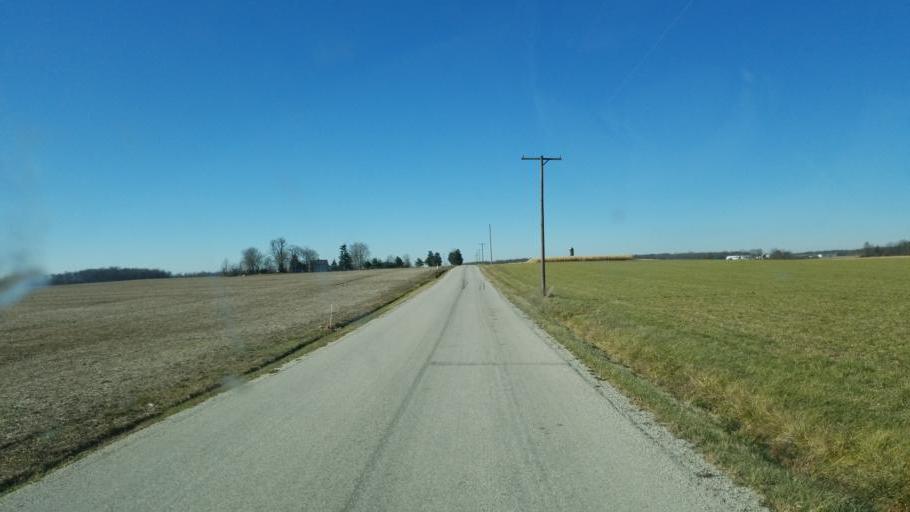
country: US
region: Ohio
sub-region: Huron County
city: Greenwich
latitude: 40.9537
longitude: -82.4789
